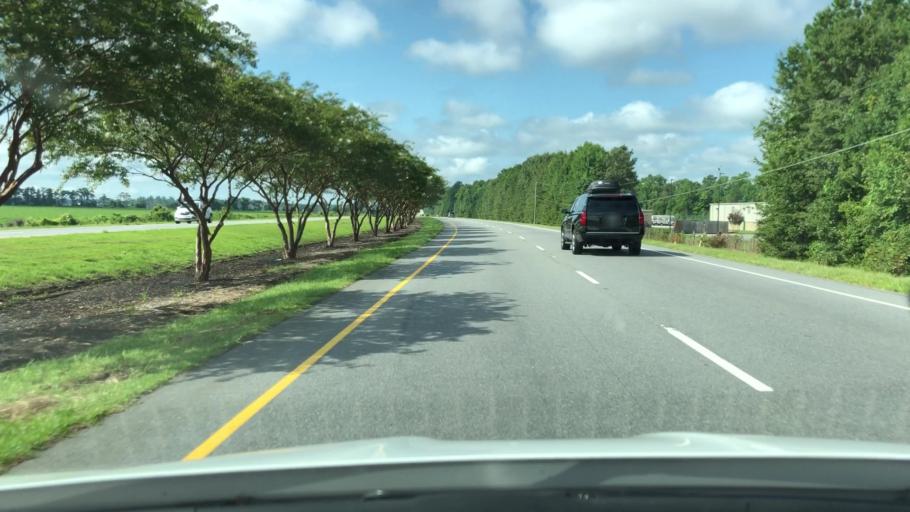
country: US
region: North Carolina
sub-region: Perquimans County
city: Hertford
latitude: 36.2025
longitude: -76.4491
